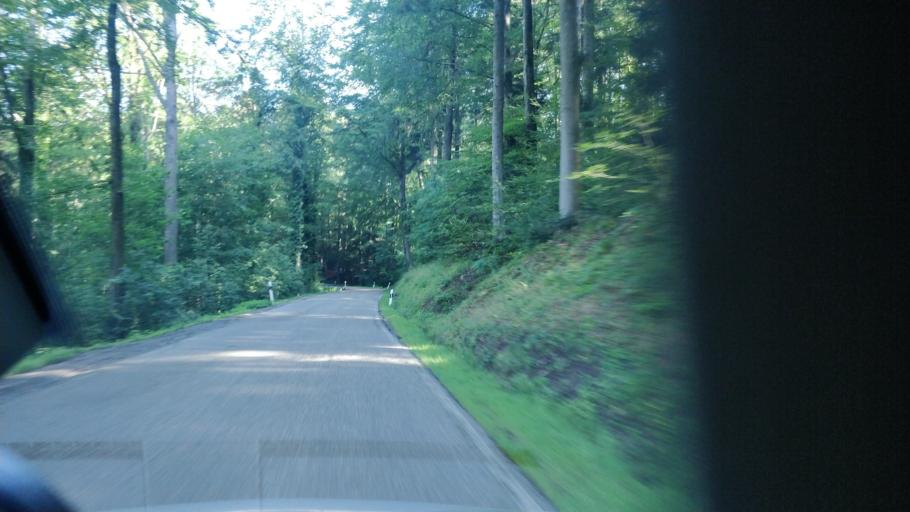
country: DE
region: Baden-Wuerttemberg
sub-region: Regierungsbezirk Stuttgart
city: Murrhardt
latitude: 49.0019
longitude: 9.5782
